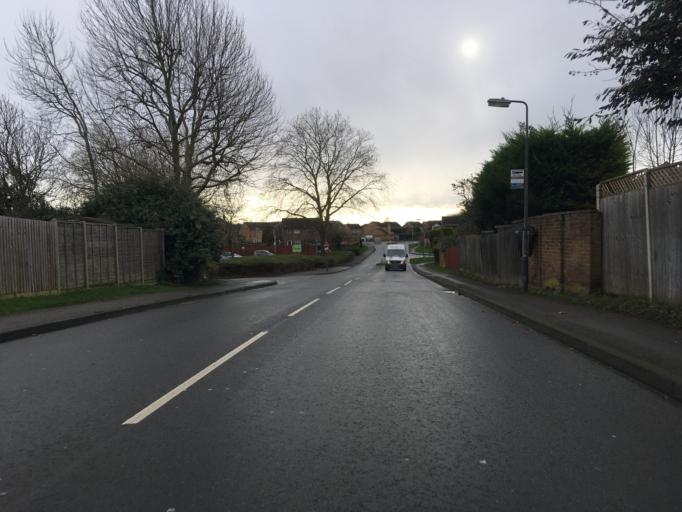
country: GB
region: England
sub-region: Worcestershire
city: Evesham
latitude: 52.0841
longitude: -1.9329
